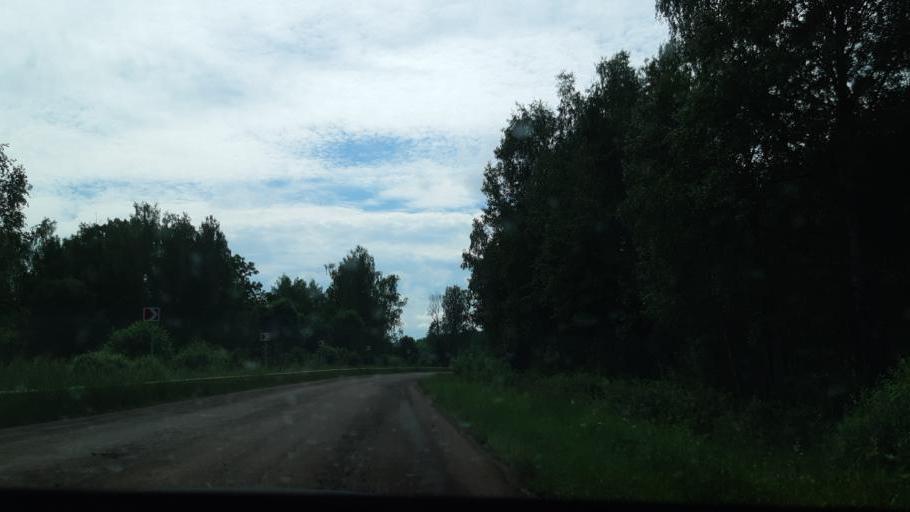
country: RU
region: Moskovskaya
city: Vereya
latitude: 55.3104
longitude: 36.1179
